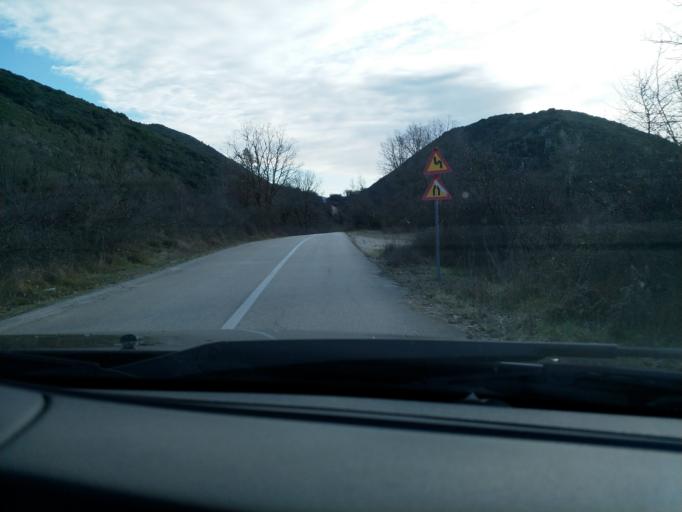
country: GR
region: Epirus
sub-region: Nomos Ioanninon
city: Asprangeloi
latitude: 39.8672
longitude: 20.7178
